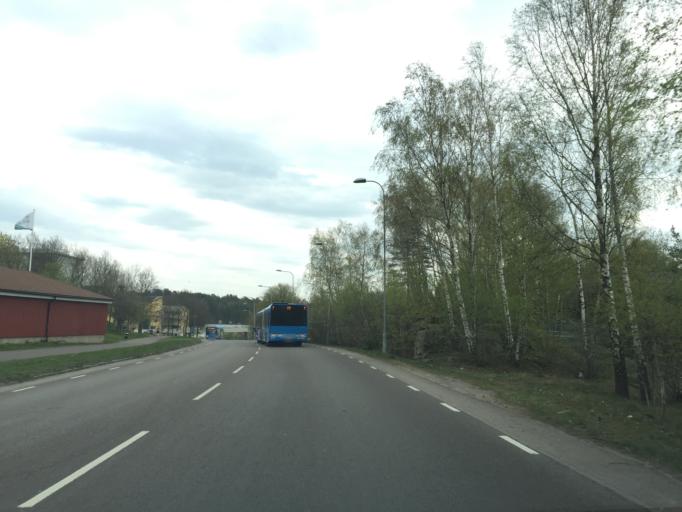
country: SE
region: Vaestra Goetaland
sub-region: Goteborg
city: Loevgaerdet
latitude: 57.8160
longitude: 12.0346
